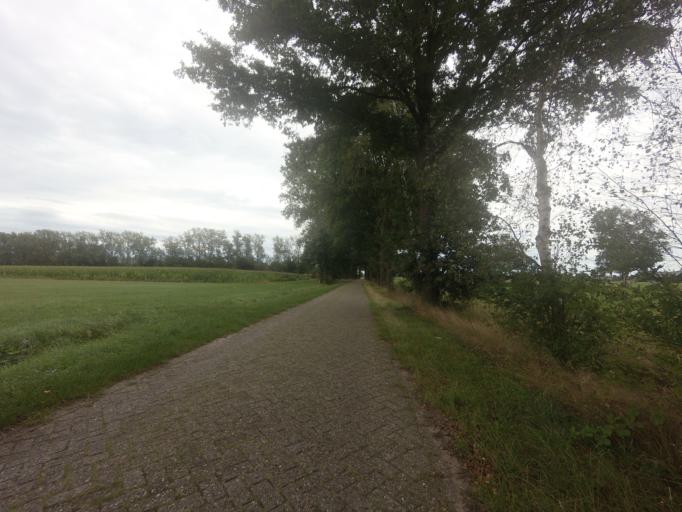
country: NL
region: Overijssel
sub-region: Gemeente Raalte
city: Raalte
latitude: 52.3531
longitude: 6.3247
